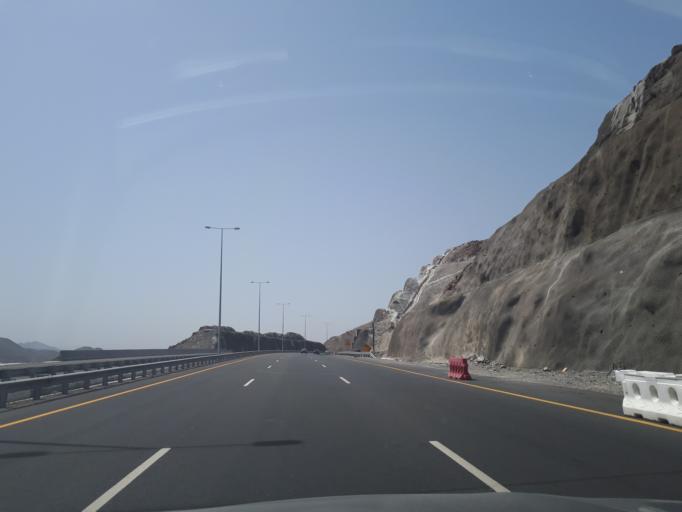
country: OM
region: Muhafazat ad Dakhiliyah
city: Bidbid
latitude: 23.3709
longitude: 58.1019
